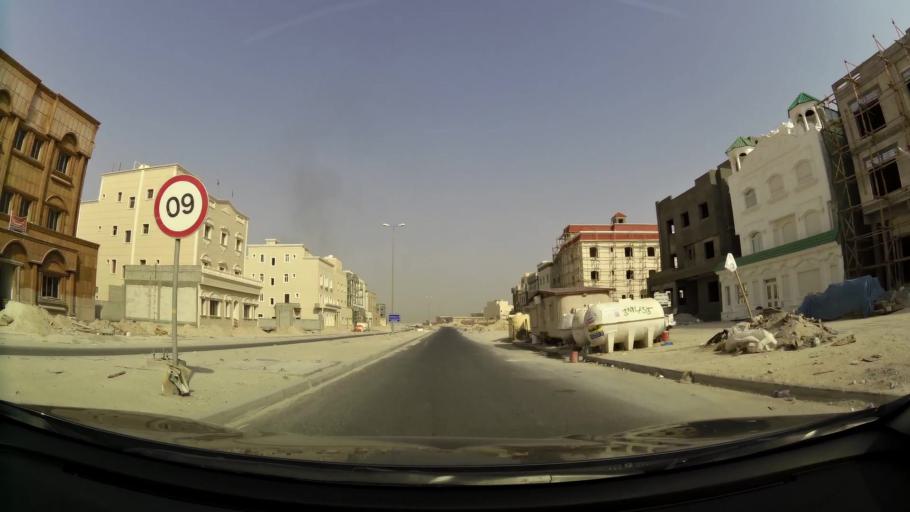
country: KW
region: Muhafazat al Jahra'
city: Al Jahra'
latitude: 29.3507
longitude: 47.7451
